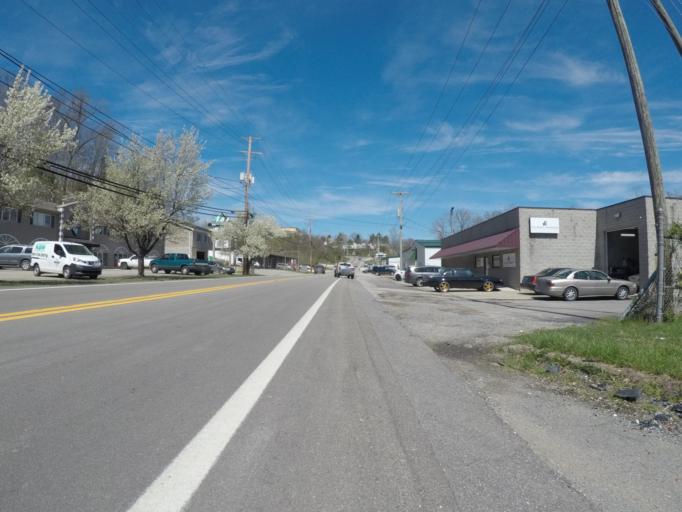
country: US
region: West Virginia
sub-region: Cabell County
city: Pea Ridge
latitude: 38.4082
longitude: -82.3202
